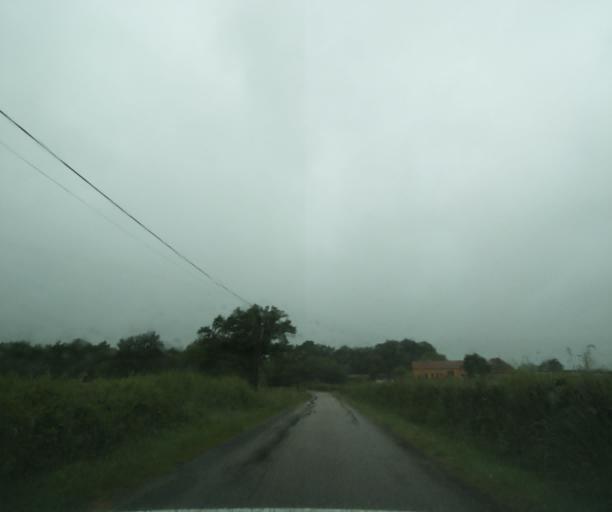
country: FR
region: Bourgogne
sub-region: Departement de Saone-et-Loire
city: Ciry-le-Noble
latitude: 46.5754
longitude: 4.3300
